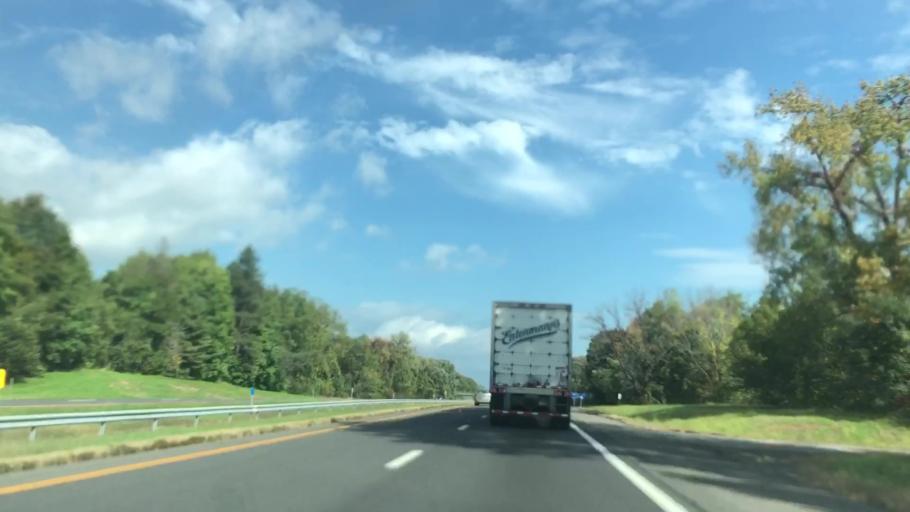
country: US
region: New York
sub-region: Ulster County
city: Glasco
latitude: 42.0345
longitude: -73.9908
